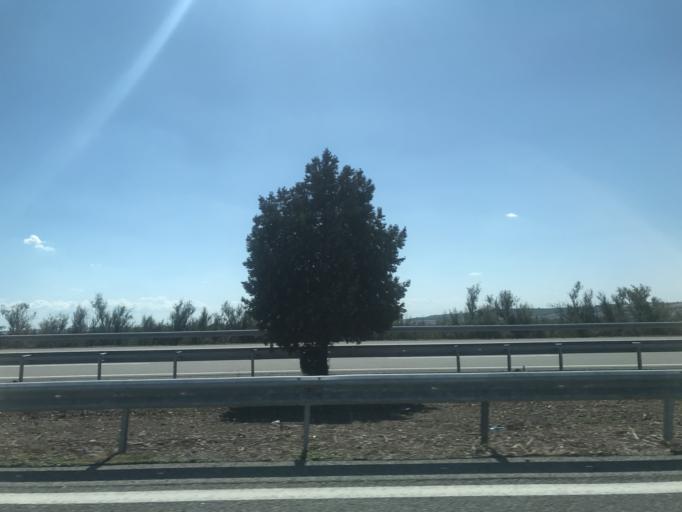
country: TR
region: Kirklareli
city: Luleburgaz
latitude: 41.4504
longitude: 27.3599
